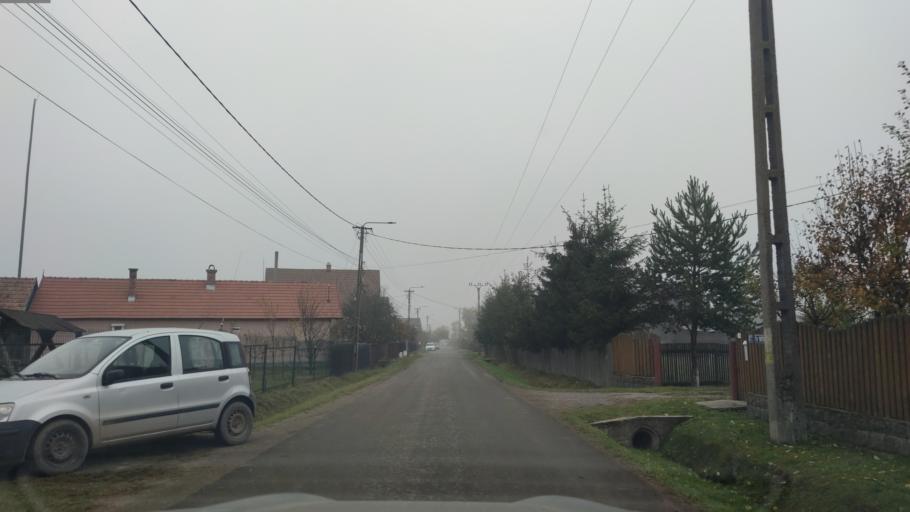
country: RO
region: Harghita
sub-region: Comuna Remetea
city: Remetea
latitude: 46.8054
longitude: 25.4421
